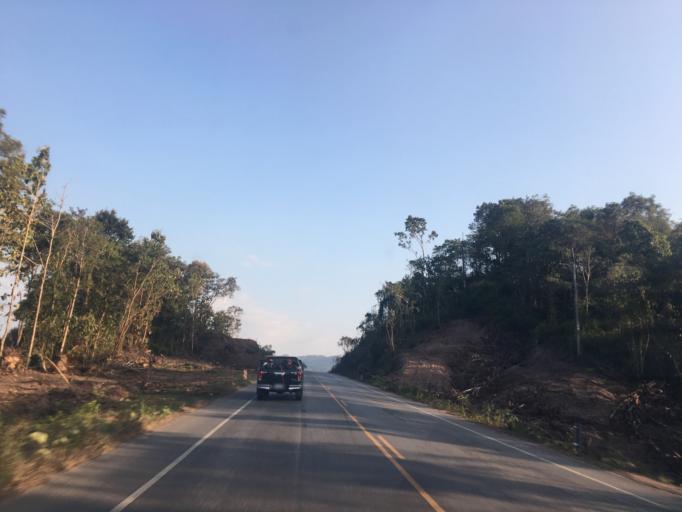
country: TH
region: Lampang
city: Ngao
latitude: 18.6223
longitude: 100.0200
